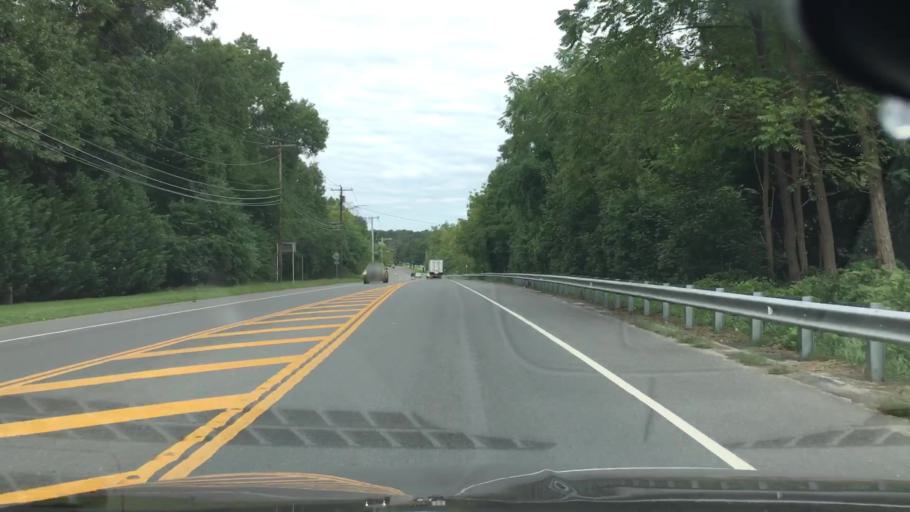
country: US
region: New York
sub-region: Suffolk County
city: Village of the Branch
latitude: 40.8495
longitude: -73.1881
